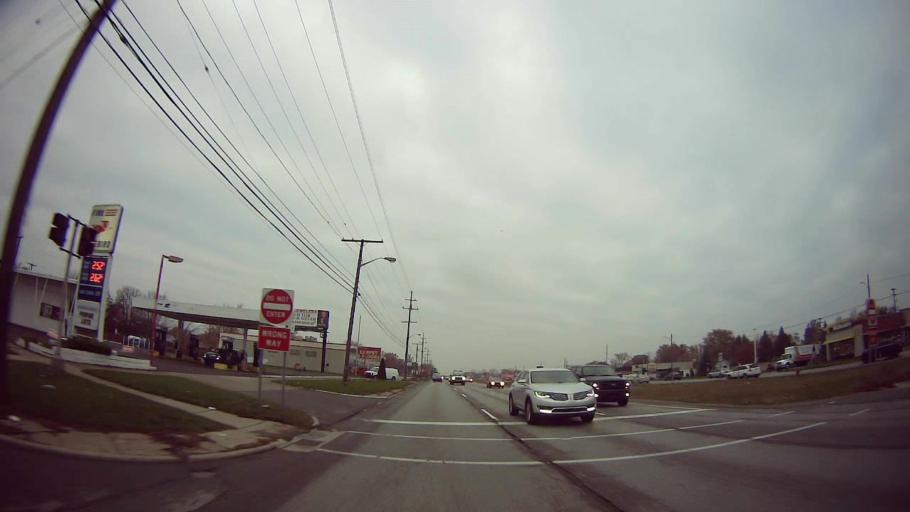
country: US
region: Michigan
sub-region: Wayne County
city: Dearborn Heights
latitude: 42.3342
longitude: -83.2732
